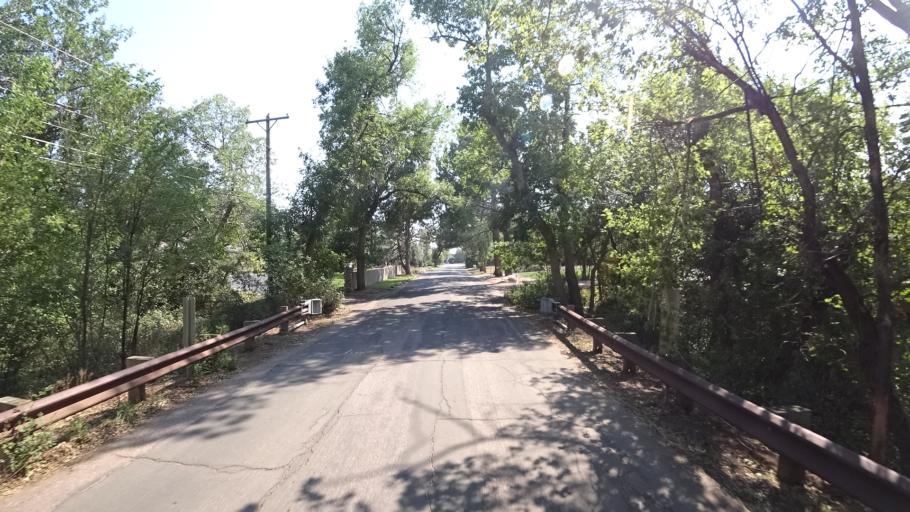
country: US
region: Colorado
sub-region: El Paso County
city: Colorado Springs
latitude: 38.7974
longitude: -104.8338
